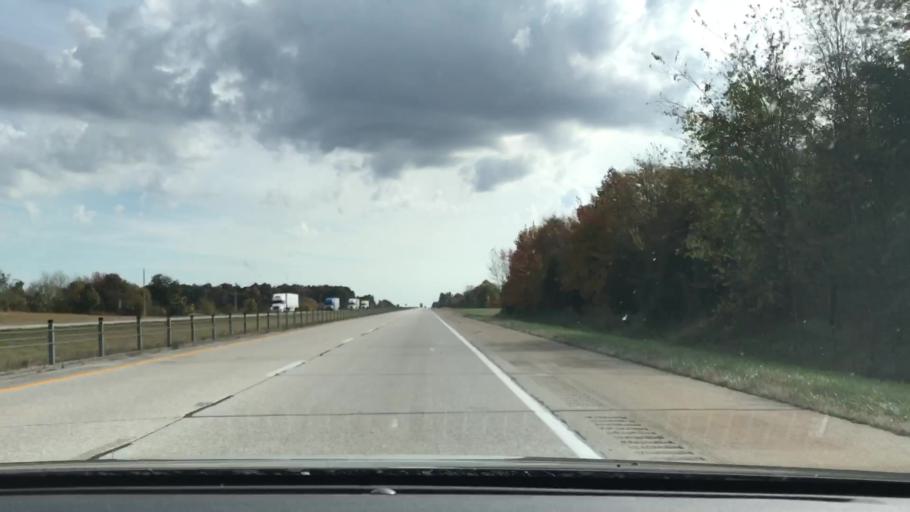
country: US
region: Kentucky
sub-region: Caldwell County
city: Princeton
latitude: 36.9964
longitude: -87.9385
